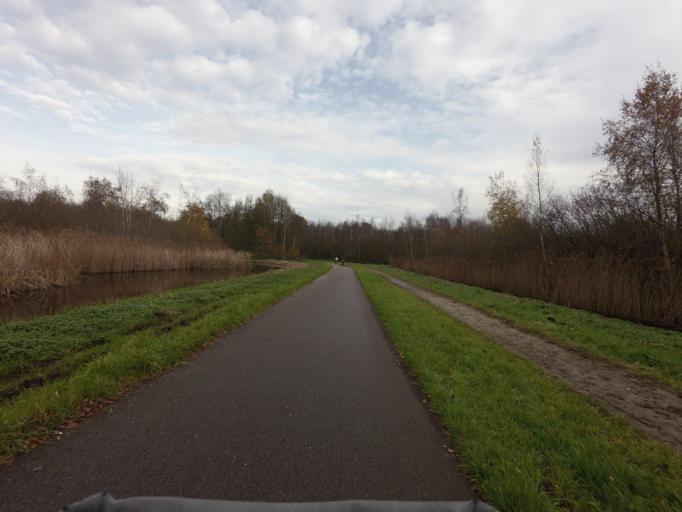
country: NL
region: North Holland
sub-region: Gemeente Amsterdam
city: Amsterdam-Zuidoost
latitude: 52.2833
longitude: 4.9683
